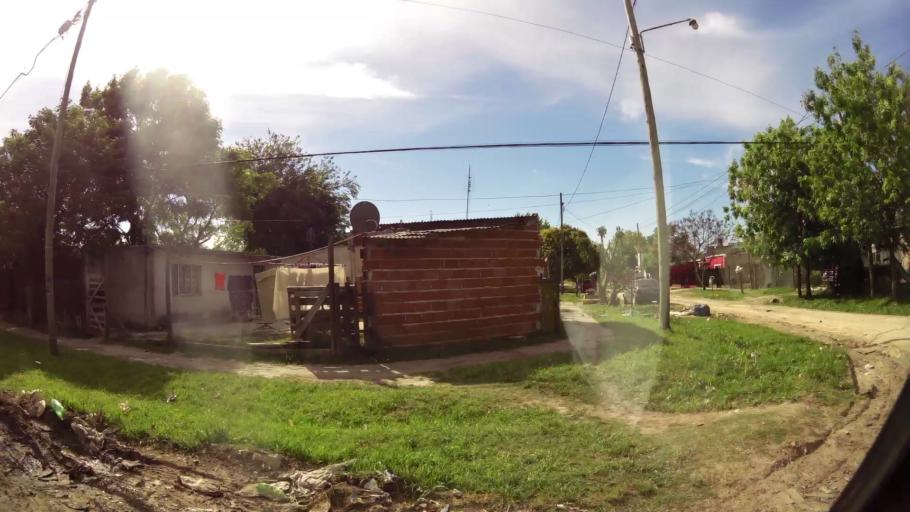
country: AR
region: Buenos Aires
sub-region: Partido de Almirante Brown
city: Adrogue
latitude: -34.8130
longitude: -58.3546
